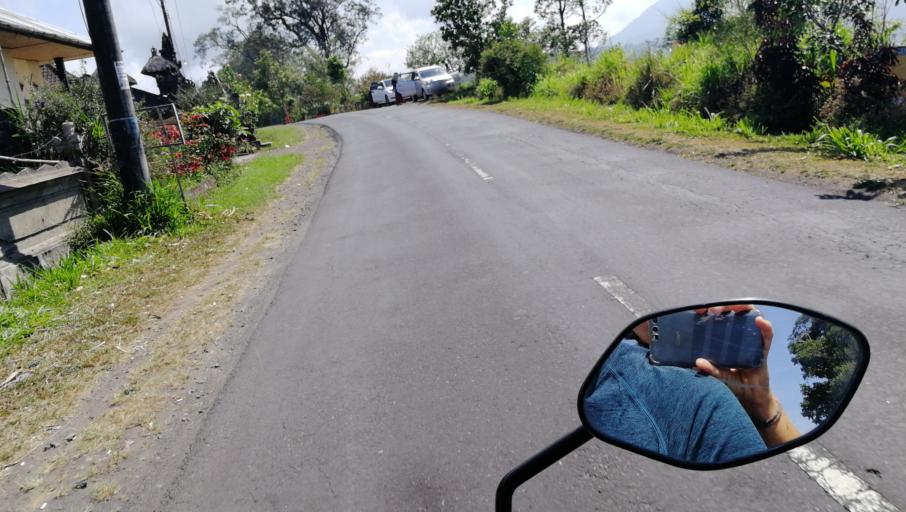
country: ID
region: Bali
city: Munduk
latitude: -8.2436
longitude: 115.1035
